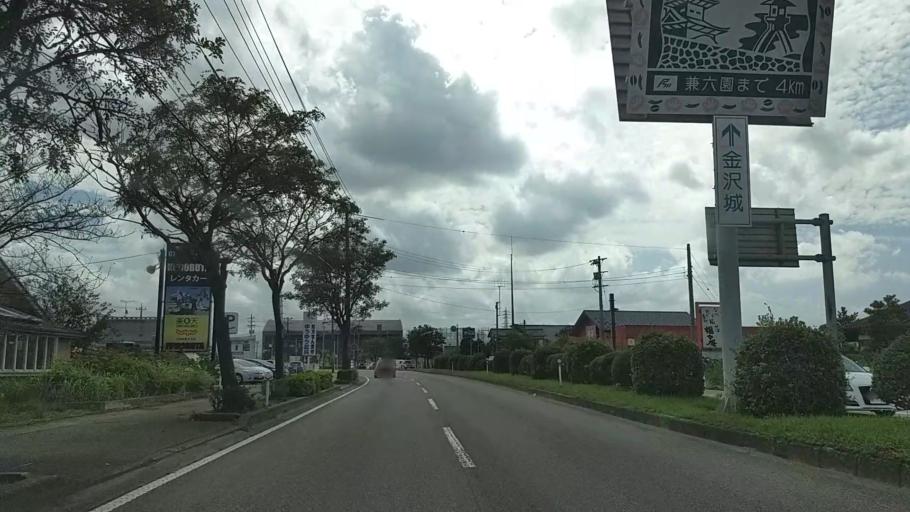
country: JP
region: Ishikawa
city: Kanazawa-shi
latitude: 36.6005
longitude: 136.6595
